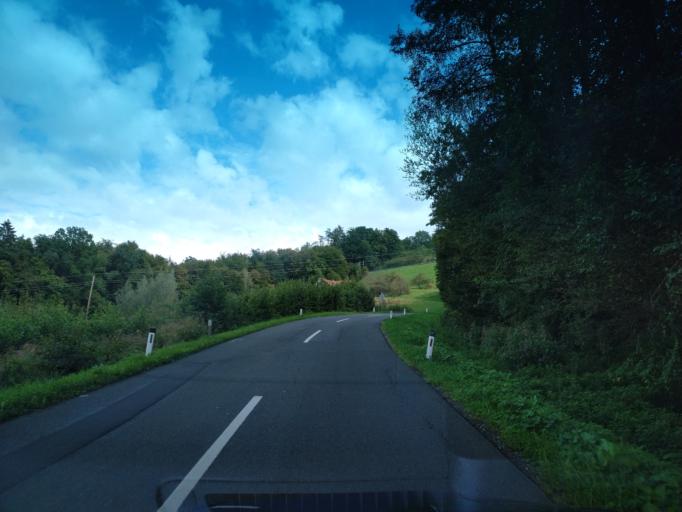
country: AT
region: Styria
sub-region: Politischer Bezirk Leibnitz
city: Seggauberg
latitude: 46.7762
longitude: 15.5196
